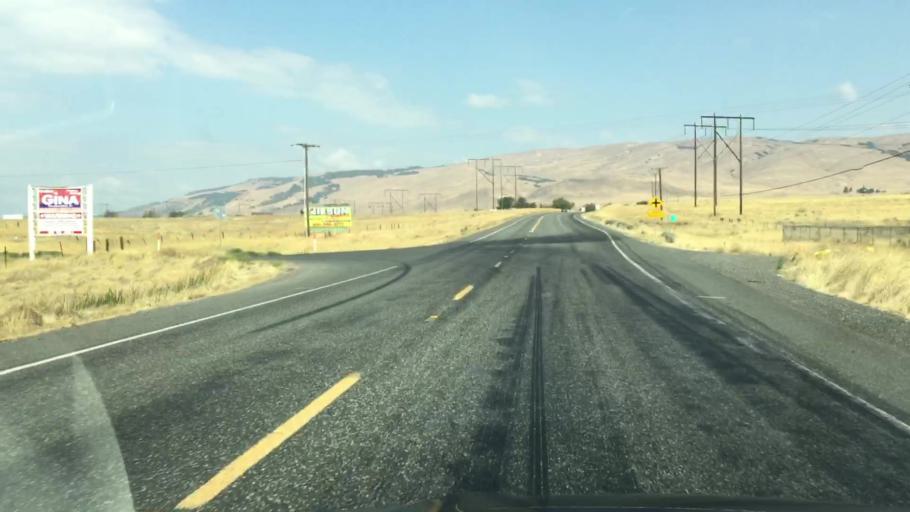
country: US
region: Washington
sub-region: Klickitat County
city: Dallesport
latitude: 45.6320
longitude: -121.1518
